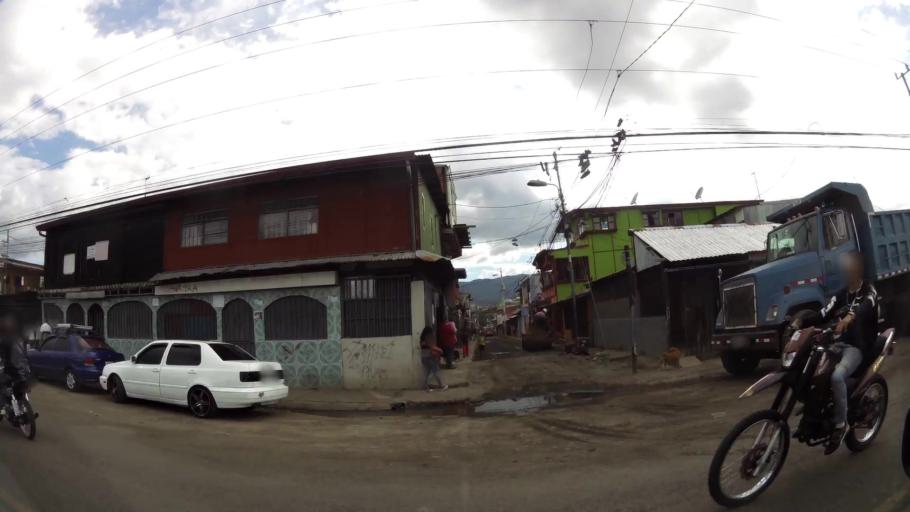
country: CR
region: San Jose
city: San Rafael
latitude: 9.9548
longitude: -84.1529
